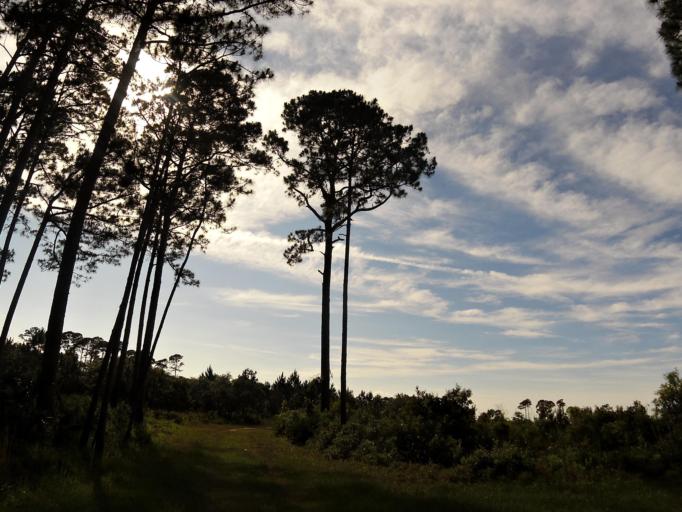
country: US
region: Florida
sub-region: Saint Johns County
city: Villano Beach
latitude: 30.0267
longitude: -81.3397
